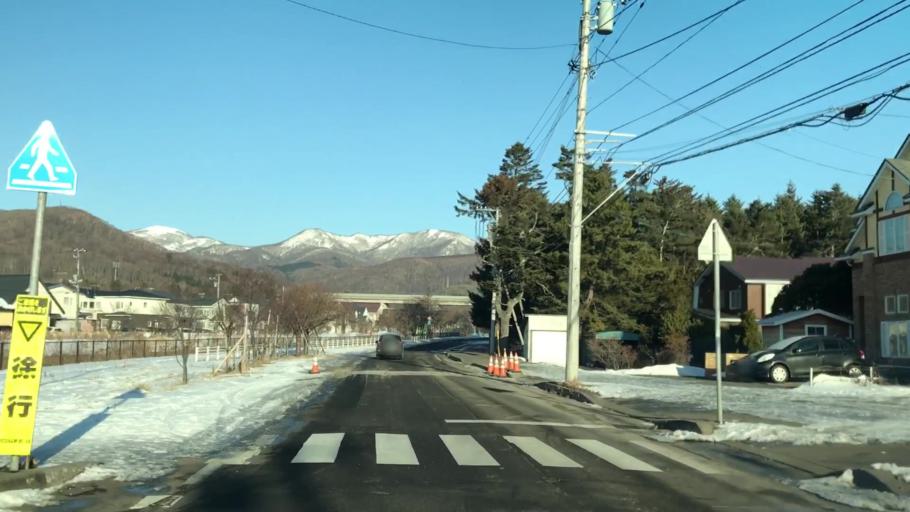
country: JP
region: Hokkaido
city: Muroran
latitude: 42.3867
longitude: 141.0700
